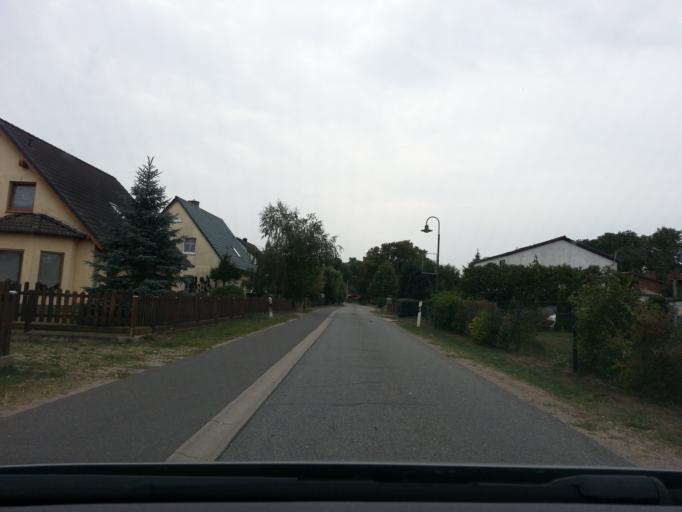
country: DE
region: Mecklenburg-Vorpommern
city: Ferdinandshof
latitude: 53.6463
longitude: 13.9203
